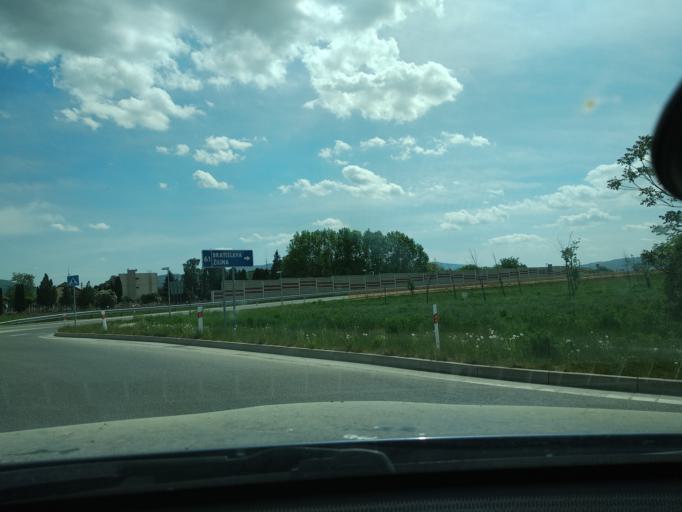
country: SK
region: Trenciansky
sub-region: Okres Trencin
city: Trencin
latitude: 48.8807
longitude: 18.0168
